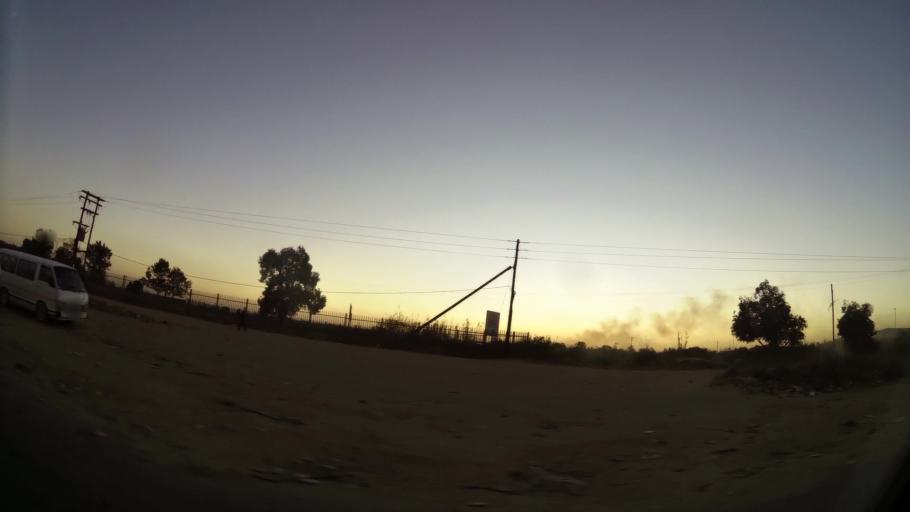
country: ZA
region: Gauteng
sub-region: City of Johannesburg Metropolitan Municipality
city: Diepsloot
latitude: -25.9433
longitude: 28.0199
